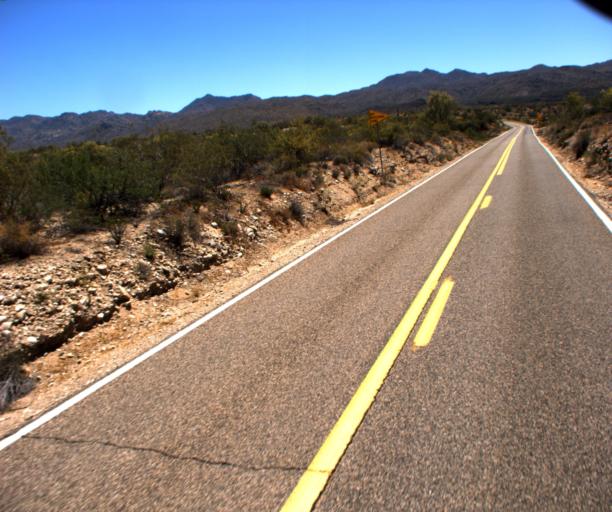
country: US
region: Arizona
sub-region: Yavapai County
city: Bagdad
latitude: 34.4882
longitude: -113.0646
